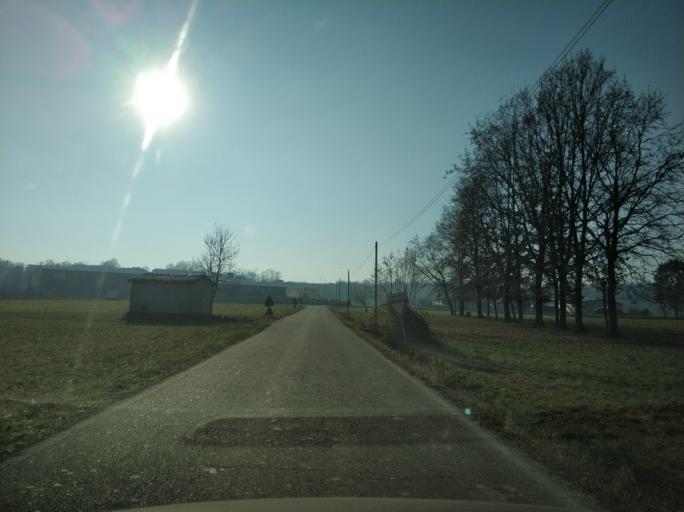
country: IT
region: Piedmont
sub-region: Provincia di Torino
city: Levone
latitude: 45.2999
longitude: 7.6148
